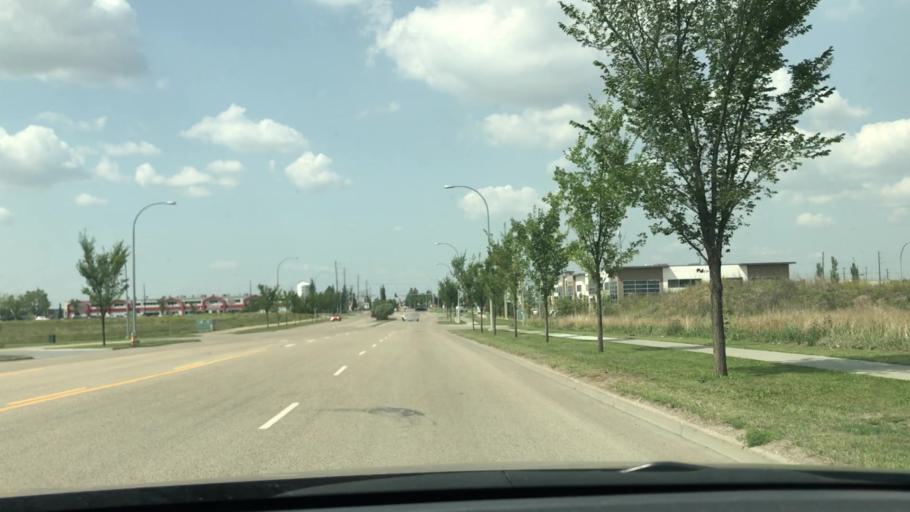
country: CA
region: Alberta
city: Edmonton
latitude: 53.4956
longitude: -113.4133
